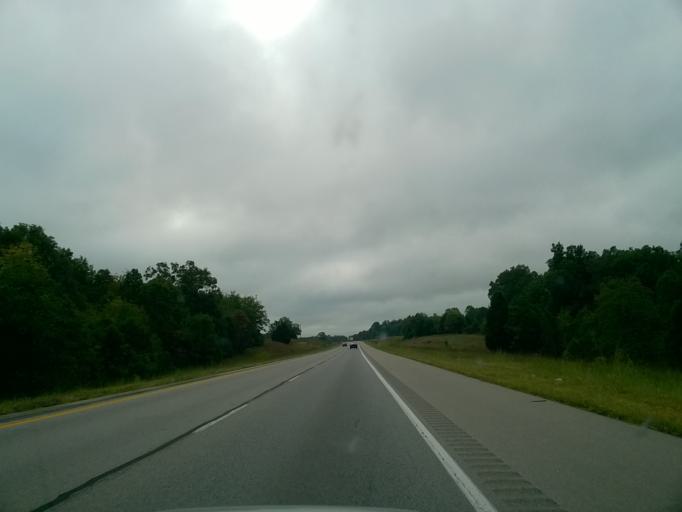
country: US
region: Indiana
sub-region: Harrison County
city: Corydon
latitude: 38.2519
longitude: -86.2776
